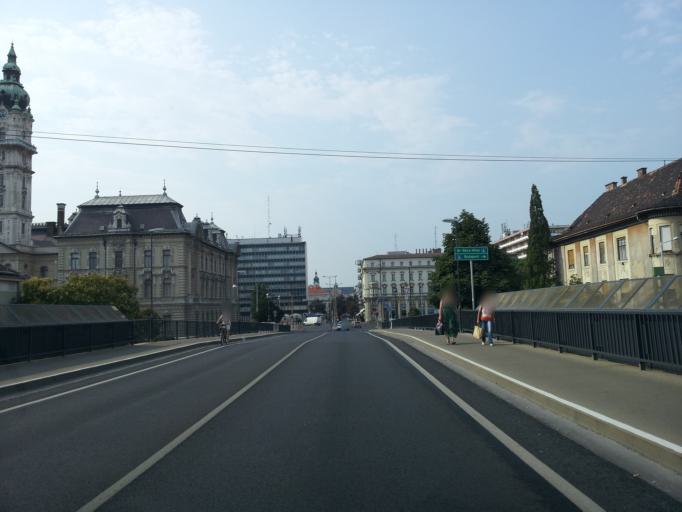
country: HU
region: Gyor-Moson-Sopron
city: Gyor
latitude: 47.6826
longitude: 17.6366
